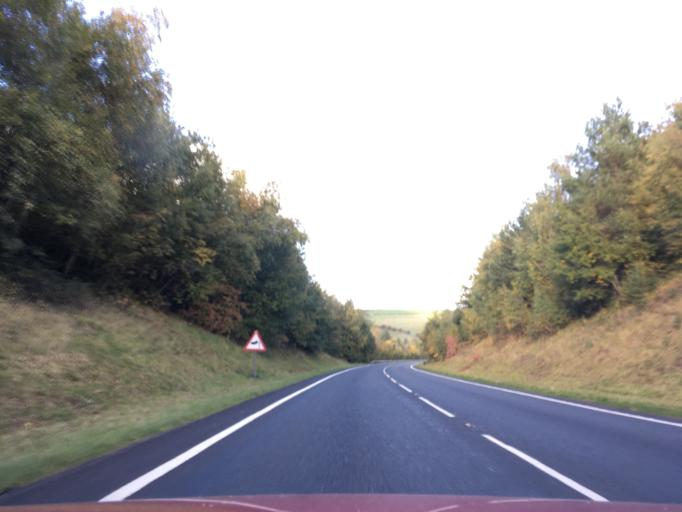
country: GB
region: Wales
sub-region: Sir Powys
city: Brecon
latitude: 51.9847
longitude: -3.3287
